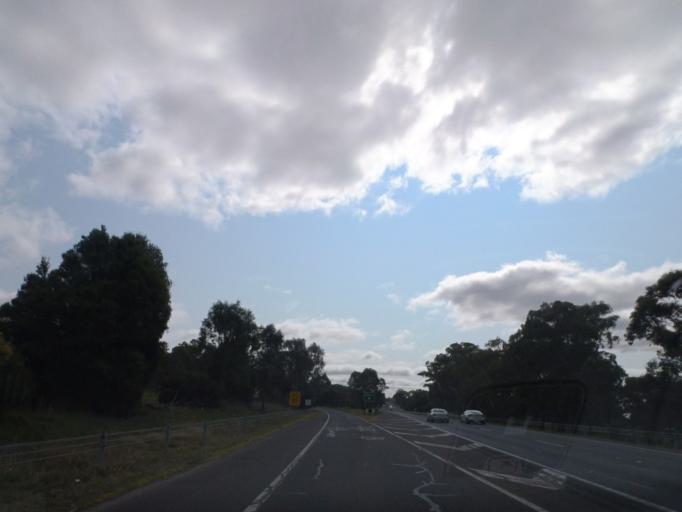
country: AU
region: Victoria
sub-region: Murrindindi
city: Kinglake West
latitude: -37.1121
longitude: 145.0916
